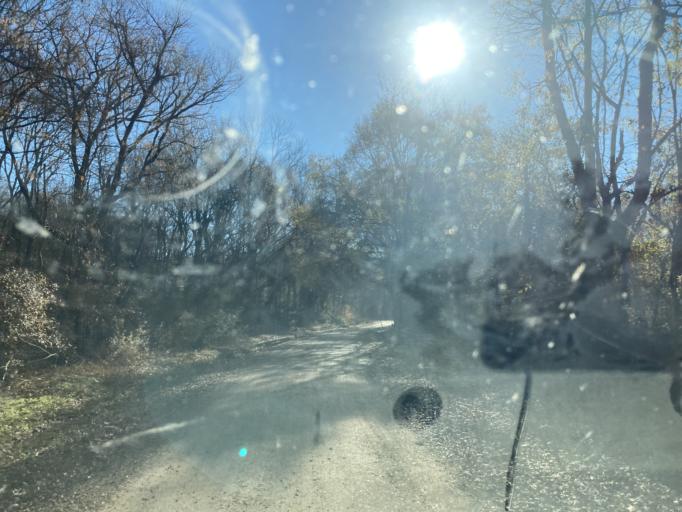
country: US
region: Mississippi
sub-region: Yazoo County
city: Yazoo City
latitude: 32.7132
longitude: -90.4171
